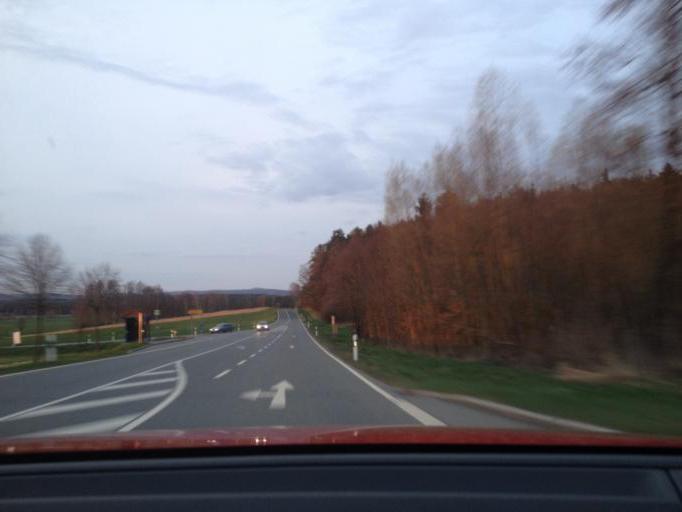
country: DE
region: Bavaria
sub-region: Upper Palatinate
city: Speinshart
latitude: 49.8350
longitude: 11.8418
